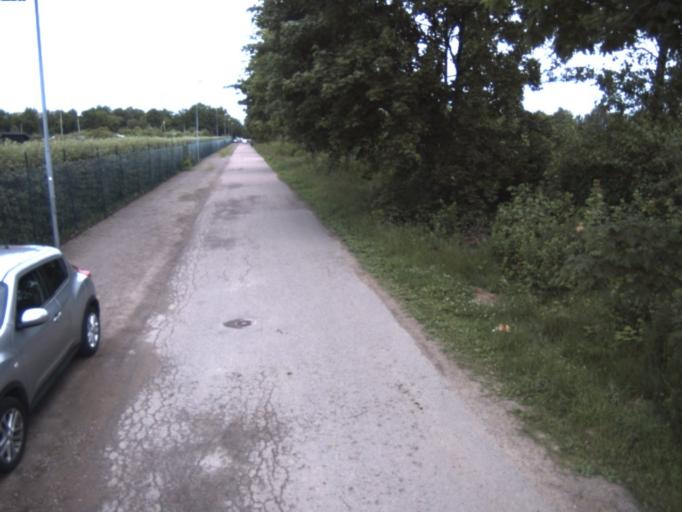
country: SE
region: Skane
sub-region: Helsingborg
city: Helsingborg
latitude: 56.0568
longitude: 12.7312
